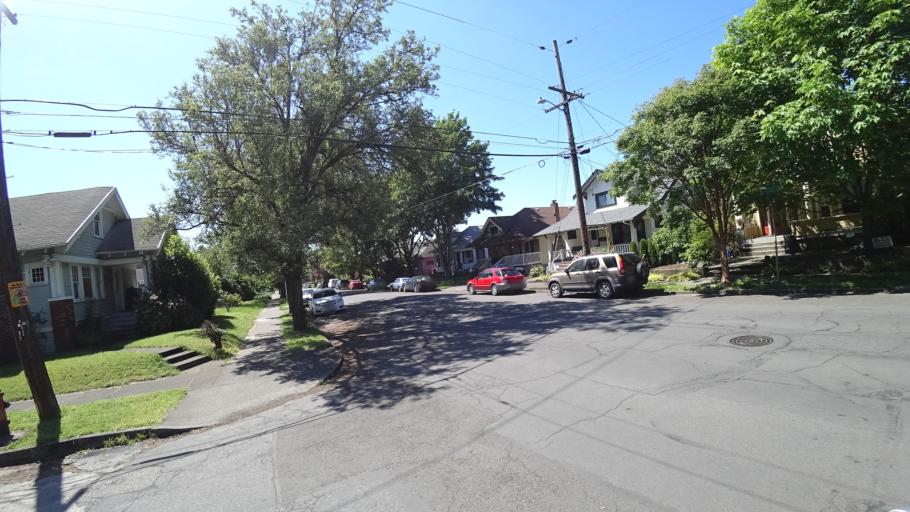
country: US
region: Oregon
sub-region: Multnomah County
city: Portland
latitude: 45.5102
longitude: -122.6257
